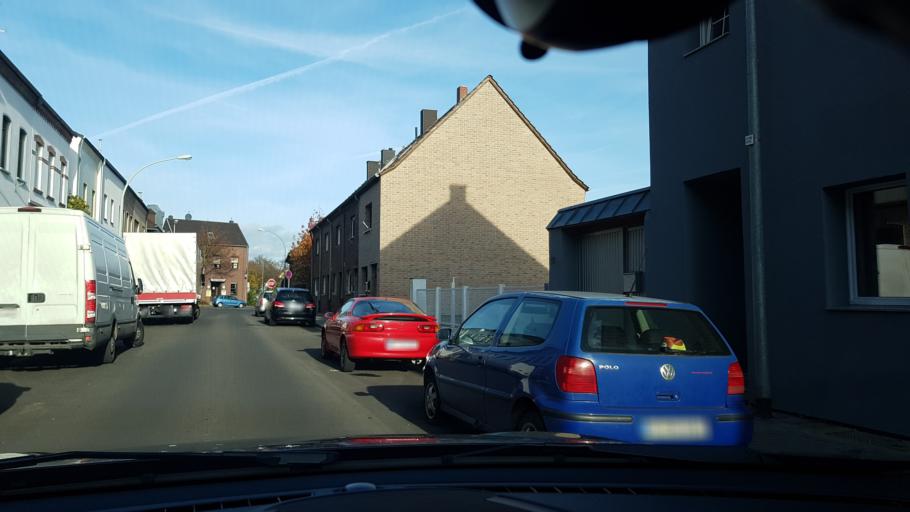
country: DE
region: North Rhine-Westphalia
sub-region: Regierungsbezirk Dusseldorf
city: Grevenbroich
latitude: 51.0947
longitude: 6.5694
